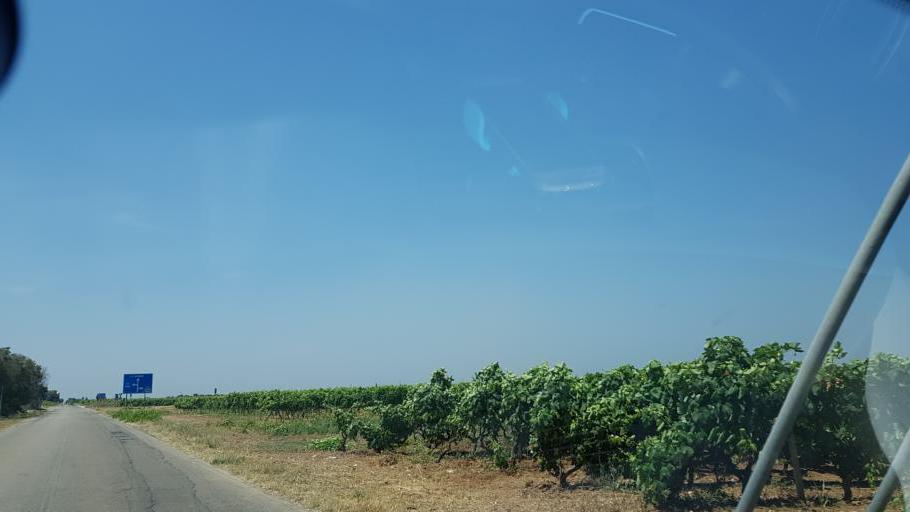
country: IT
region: Apulia
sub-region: Provincia di Brindisi
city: San Donaci
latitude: 40.4840
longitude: 17.8862
